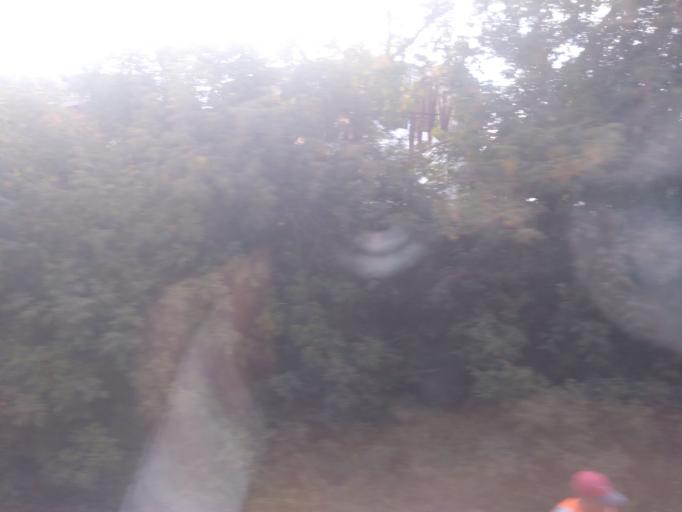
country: RU
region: Tatarstan
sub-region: Gorod Kazan'
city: Kazan
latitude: 55.8036
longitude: 49.0613
